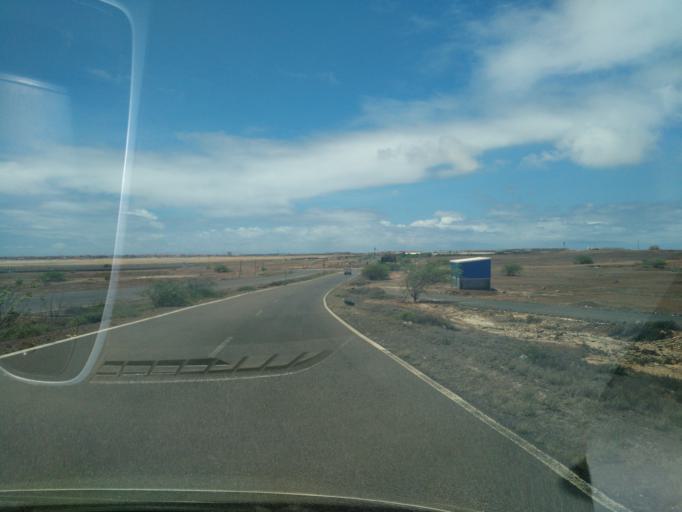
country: CV
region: Sal
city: Santa Maria
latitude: 16.6316
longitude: -22.9168
